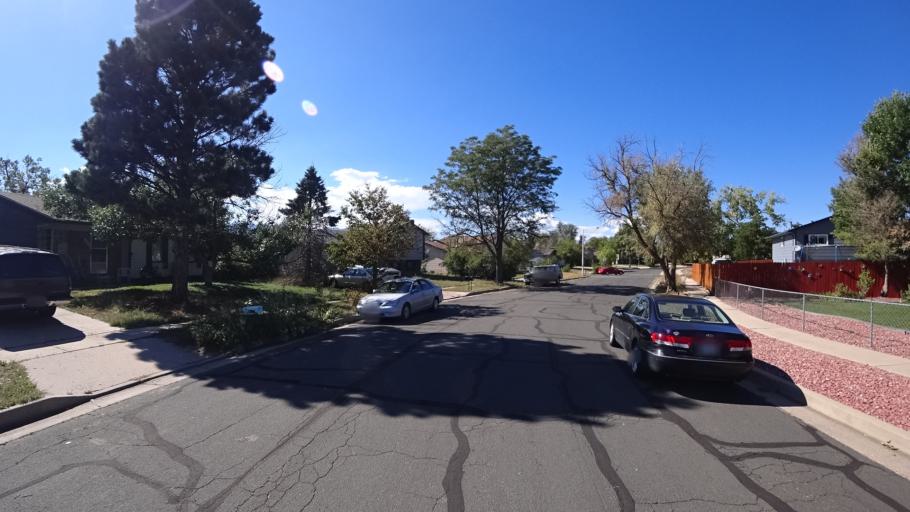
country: US
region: Colorado
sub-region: El Paso County
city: Stratmoor
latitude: 38.7906
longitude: -104.7461
